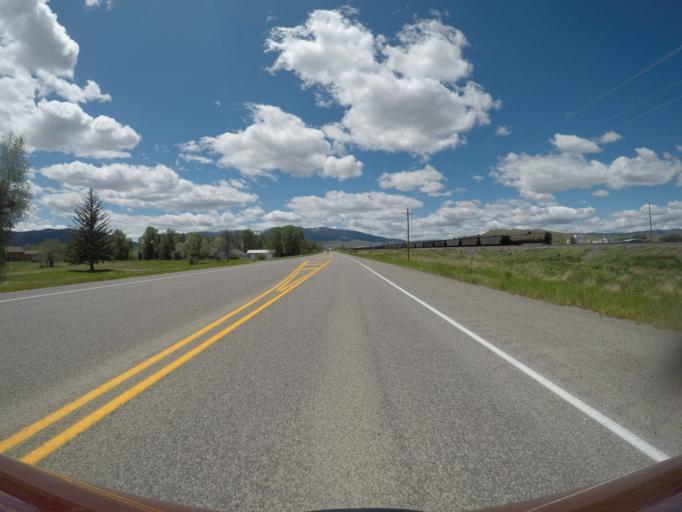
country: US
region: Montana
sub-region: Park County
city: Livingston
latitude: 45.6731
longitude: -110.5413
